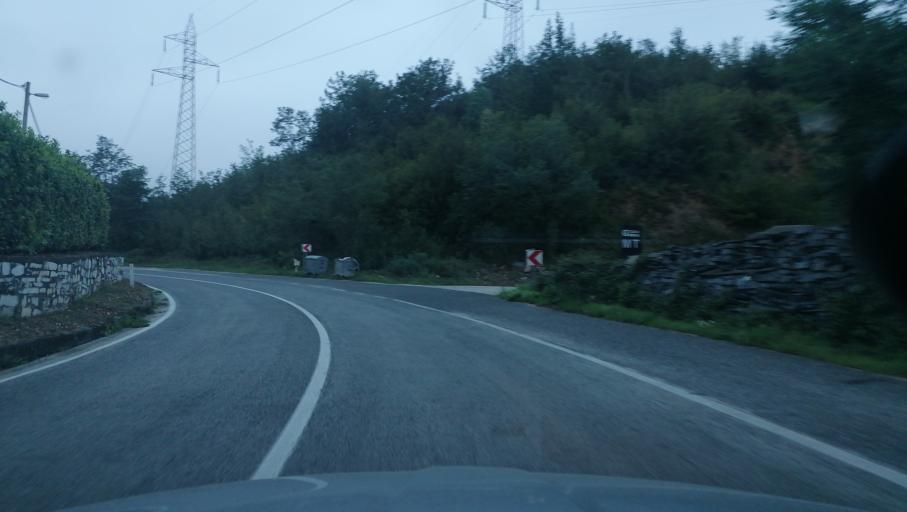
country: BA
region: Federation of Bosnia and Herzegovina
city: Jablanica
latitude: 43.7002
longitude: 17.7291
